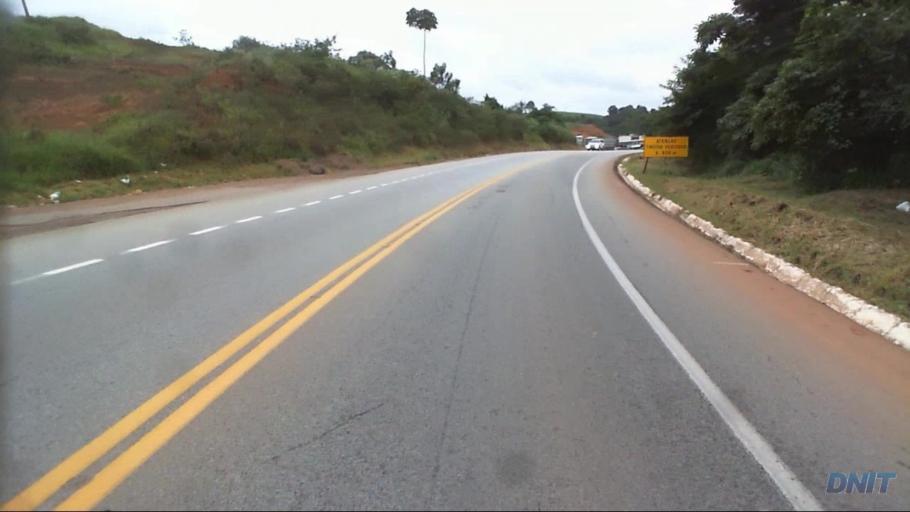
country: BR
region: Minas Gerais
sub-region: Joao Monlevade
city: Joao Monlevade
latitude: -19.8518
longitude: -43.2141
